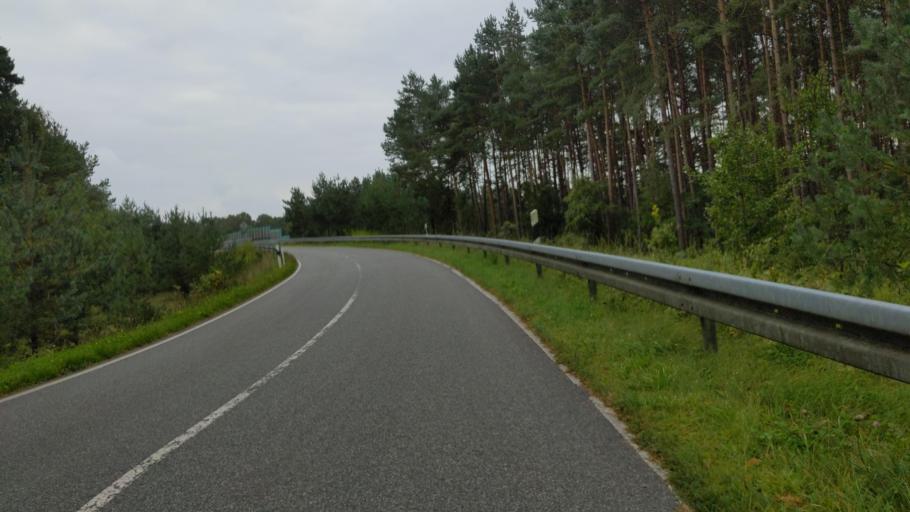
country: DE
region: Schleswig-Holstein
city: Gross Gronau
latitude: 53.8164
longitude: 10.7875
